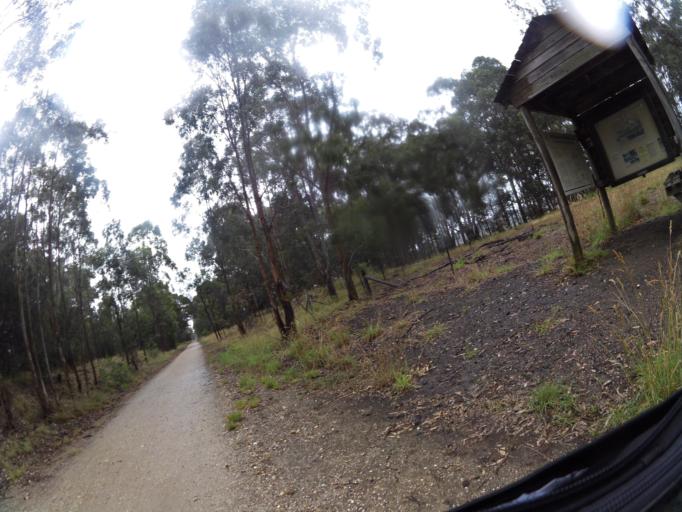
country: AU
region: Victoria
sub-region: East Gippsland
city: Lakes Entrance
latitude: -37.7942
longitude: 147.8285
